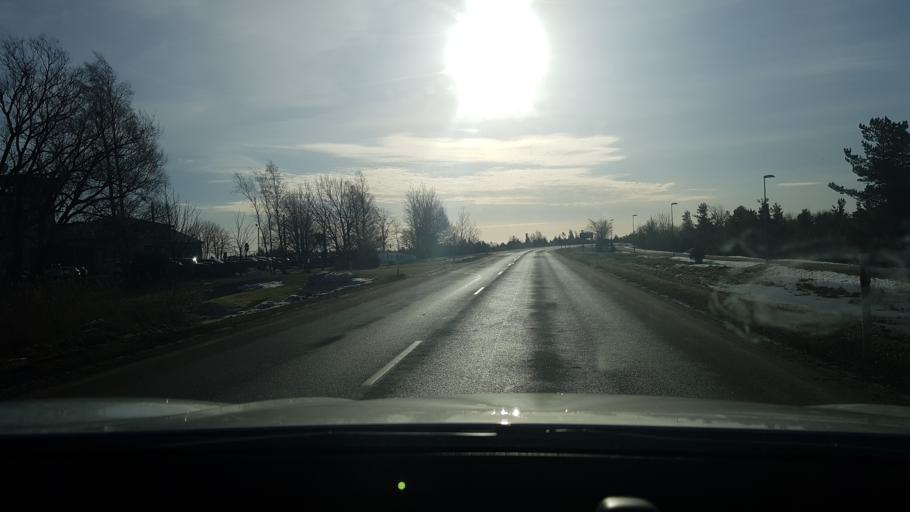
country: EE
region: Saare
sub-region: Kuressaare linn
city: Kuressaare
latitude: 58.2328
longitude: 22.5029
